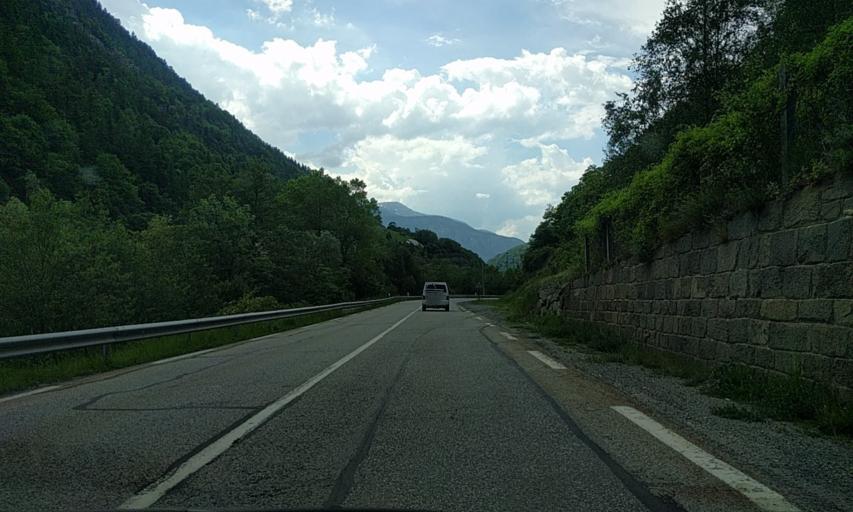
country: FR
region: Rhone-Alpes
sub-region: Departement de la Savoie
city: Saint-Michel-de-Maurienne
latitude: 45.2080
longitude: 6.5224
